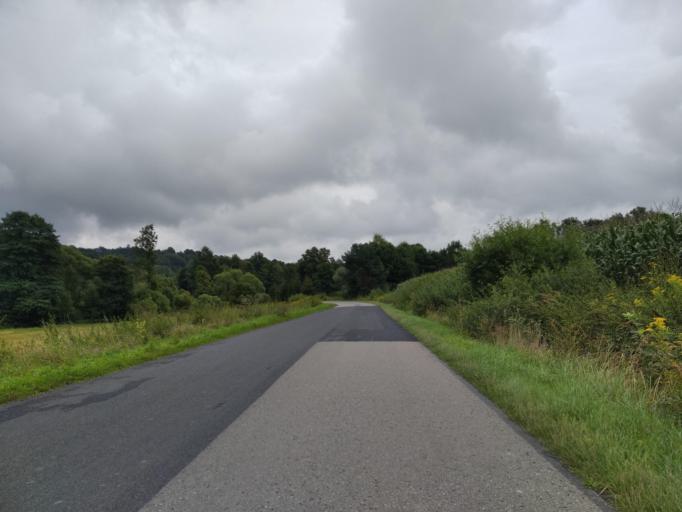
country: PL
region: Subcarpathian Voivodeship
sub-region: Powiat brzozowski
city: Nozdrzec
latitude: 49.7264
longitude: 22.2807
